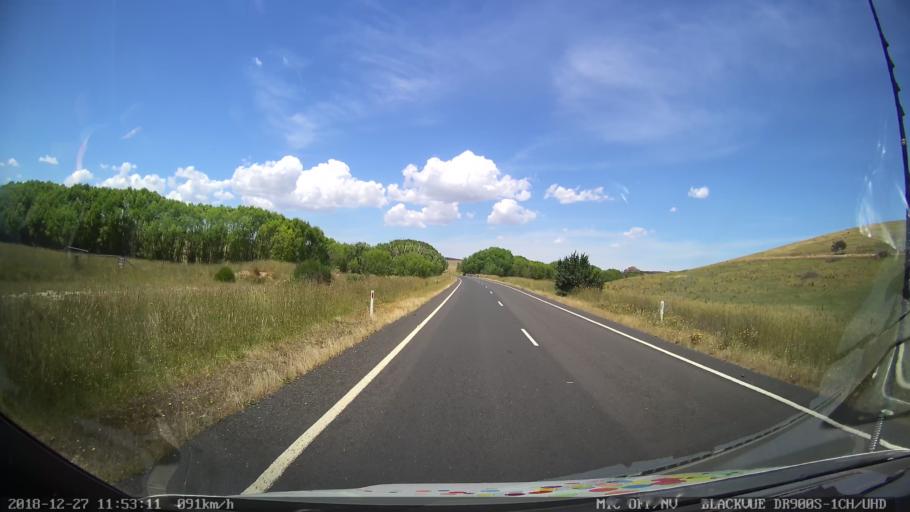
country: AU
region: New South Wales
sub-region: Blayney
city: Blayney
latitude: -33.6584
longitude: 149.4027
